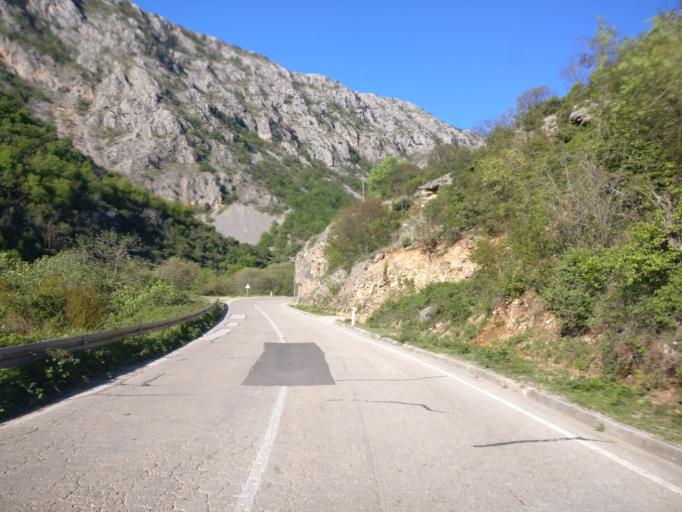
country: BA
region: Federation of Bosnia and Herzegovina
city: Stolac
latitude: 43.0725
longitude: 18.0401
